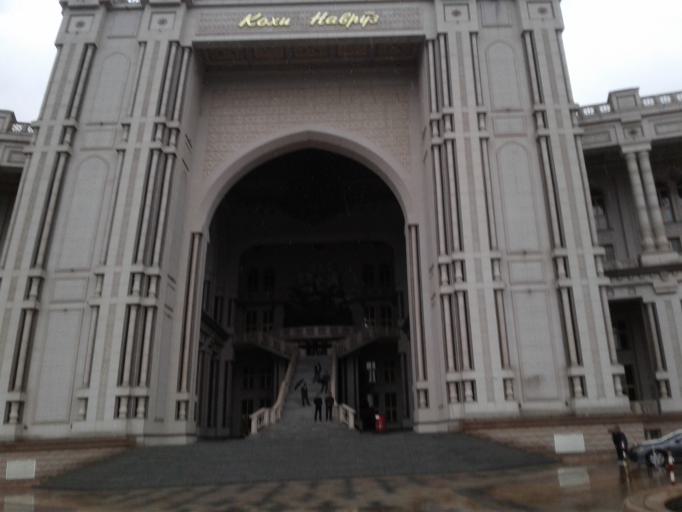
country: TJ
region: Dushanbe
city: Dushanbe
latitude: 38.5835
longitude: 68.7688
